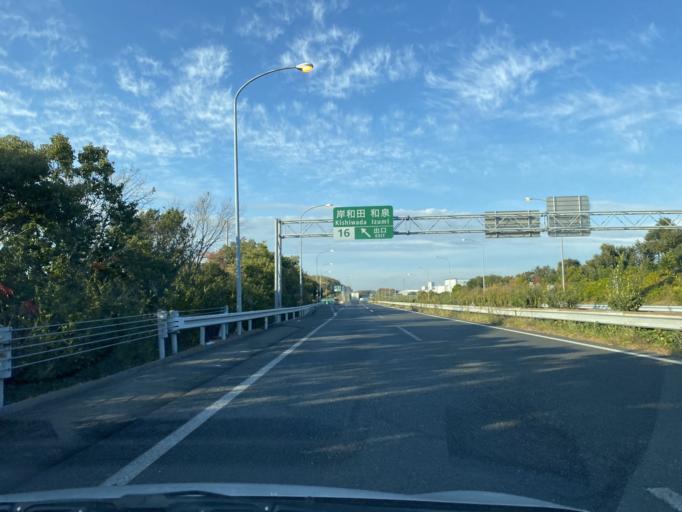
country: JP
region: Osaka
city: Izumi
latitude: 34.4342
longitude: 135.4456
